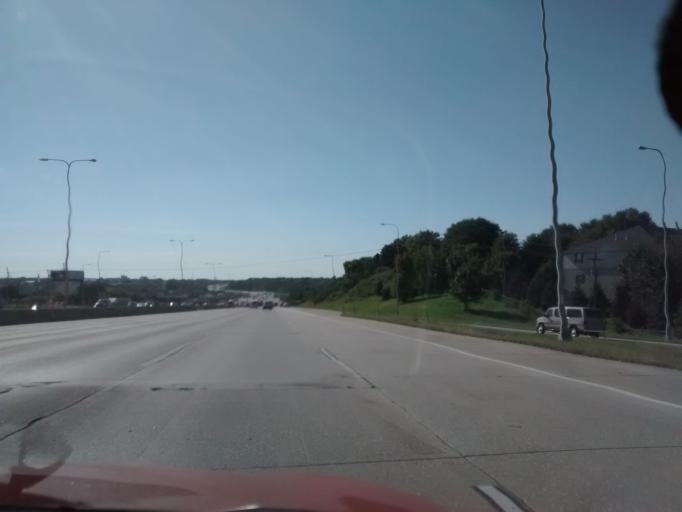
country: US
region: Nebraska
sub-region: Douglas County
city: Ralston
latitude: 41.2240
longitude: -96.0262
